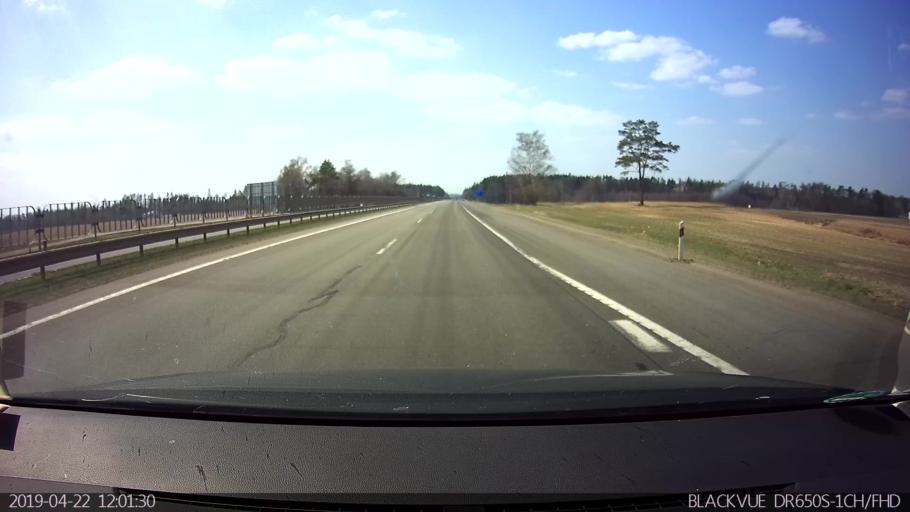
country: BY
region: Minsk
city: Pryvol'ny
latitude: 53.8016
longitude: 27.7813
